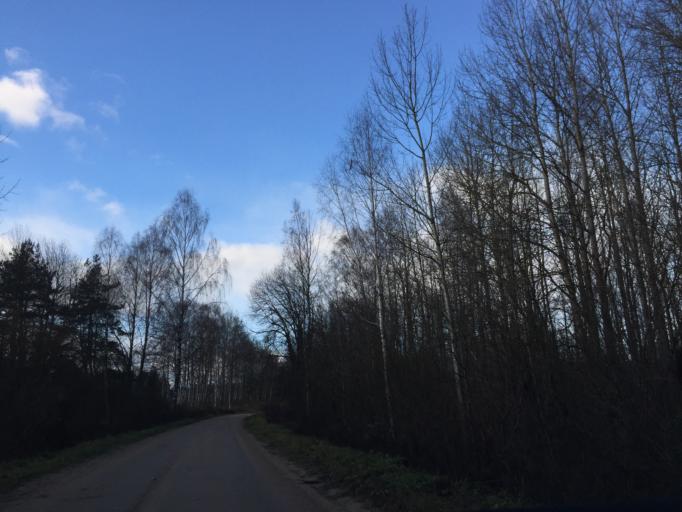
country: LV
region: Valmieras Rajons
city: Valmiera
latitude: 57.5382
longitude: 25.3830
